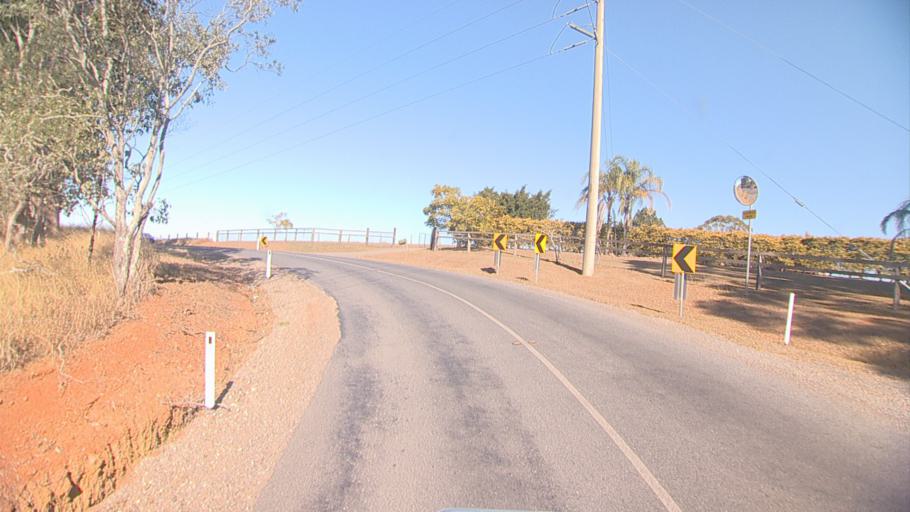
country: AU
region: Queensland
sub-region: Logan
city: Cedar Vale
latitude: -27.8957
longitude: 153.0144
